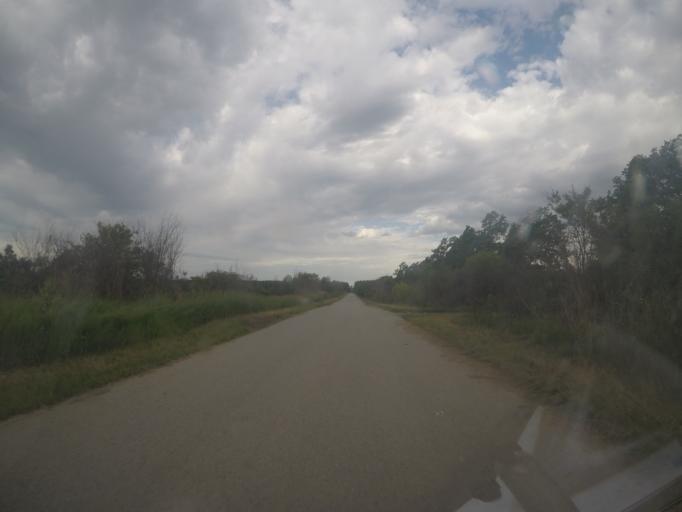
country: RS
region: Central Serbia
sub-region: Belgrade
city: Zemun
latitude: 44.8937
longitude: 20.3863
